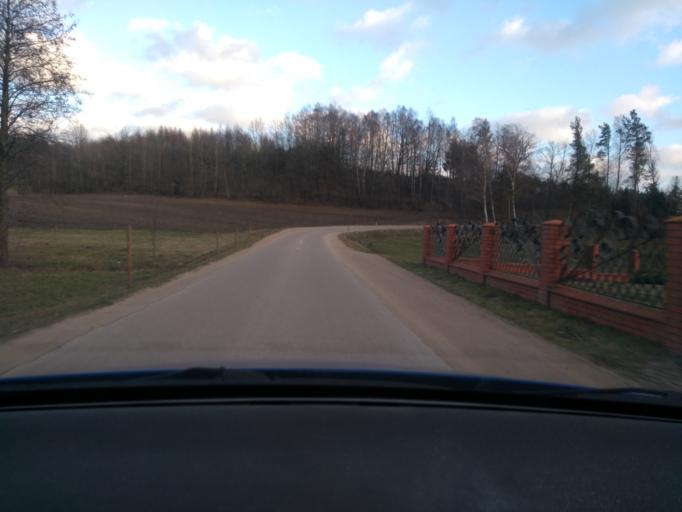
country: PL
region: Pomeranian Voivodeship
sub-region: Powiat kartuski
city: Przodkowo
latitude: 54.4150
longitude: 18.2493
